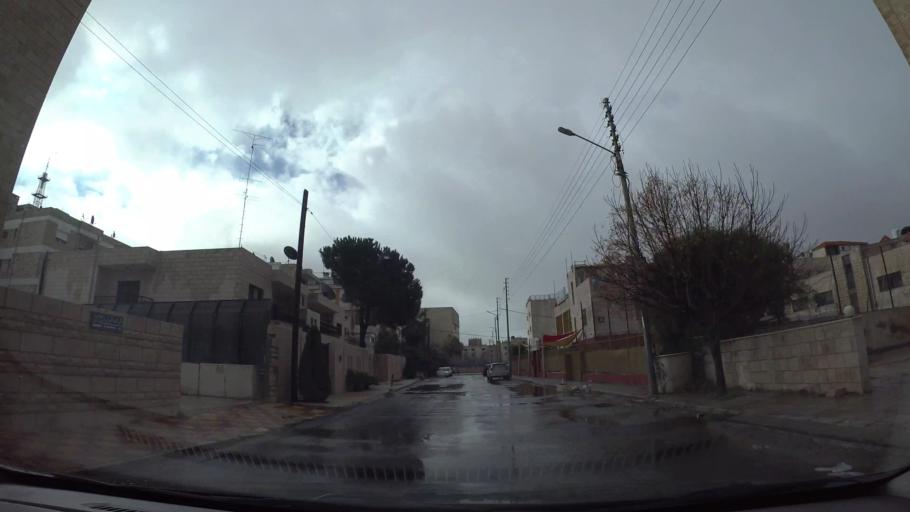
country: JO
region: Amman
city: Wadi as Sir
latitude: 31.9617
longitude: 35.8612
